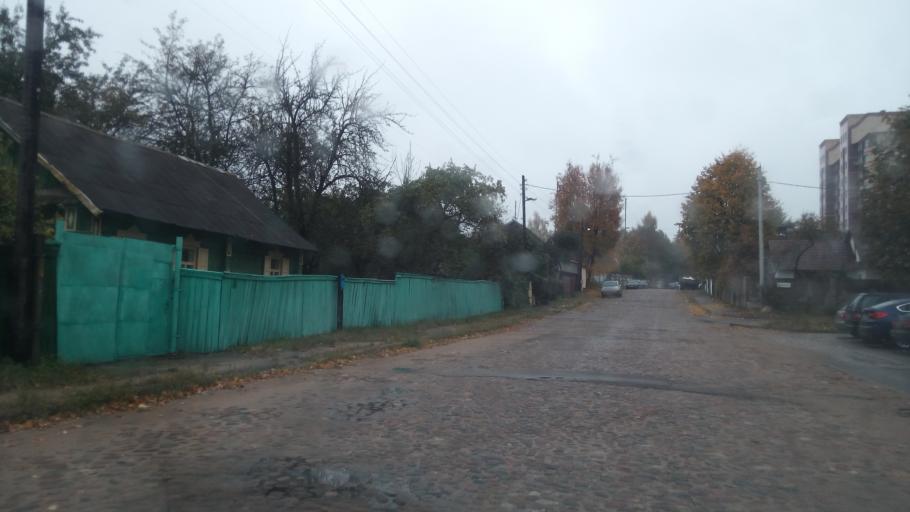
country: BY
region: Minsk
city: Minsk
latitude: 53.9370
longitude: 27.5908
